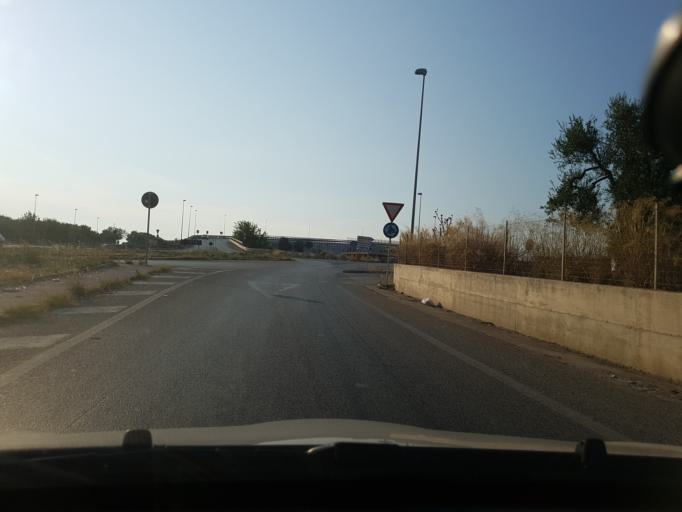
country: IT
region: Apulia
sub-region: Provincia di Foggia
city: Cerignola
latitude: 41.2731
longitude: 15.8765
